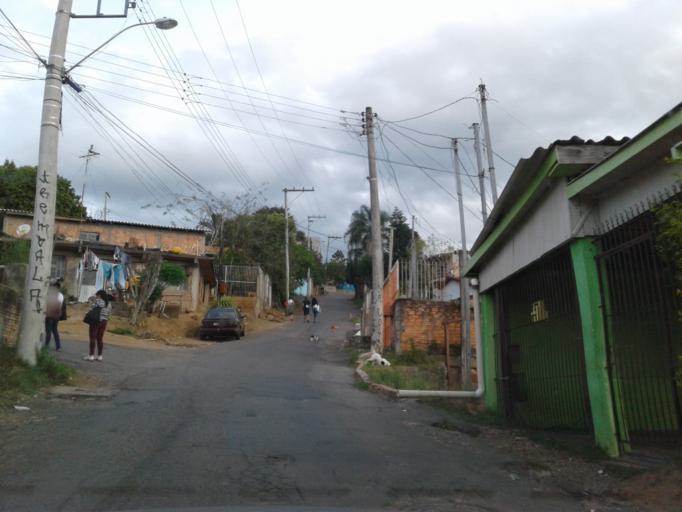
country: BR
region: Rio Grande do Sul
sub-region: Porto Alegre
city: Porto Alegre
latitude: -30.0610
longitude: -51.1458
